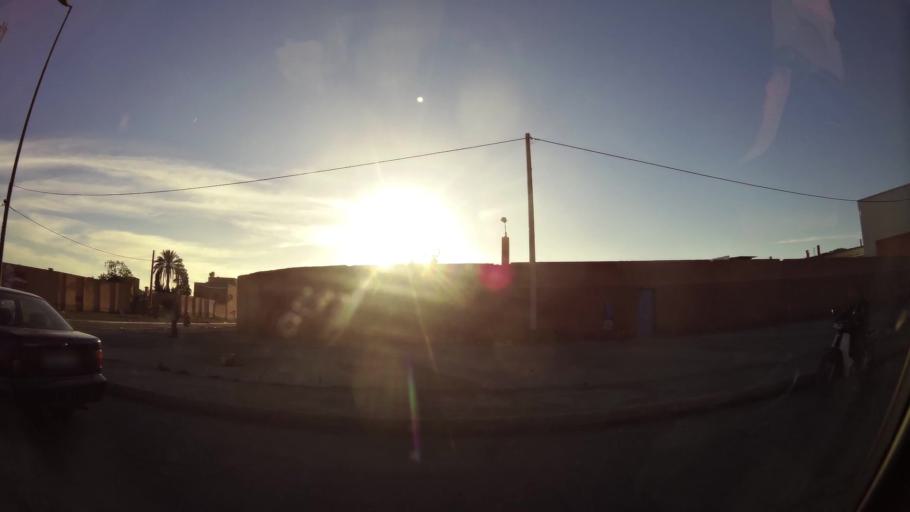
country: MA
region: Marrakech-Tensift-Al Haouz
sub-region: Marrakech
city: Marrakesh
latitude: 31.6249
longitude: -8.0432
